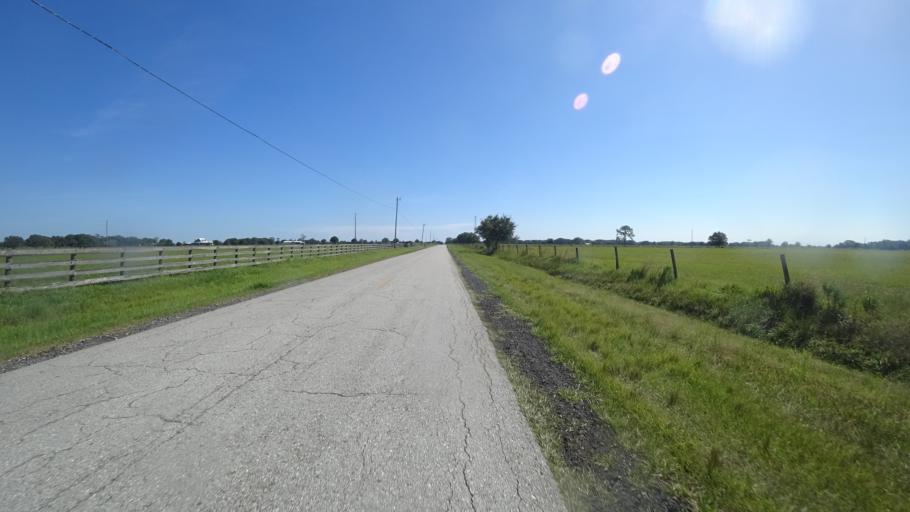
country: US
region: Florida
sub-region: Sarasota County
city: Warm Mineral Springs
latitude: 27.2739
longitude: -82.1928
